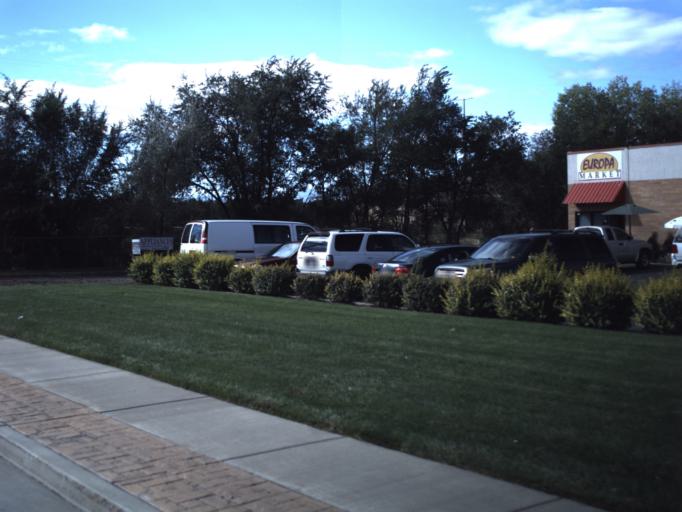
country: US
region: Utah
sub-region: Salt Lake County
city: Taylorsville
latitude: 40.7083
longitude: -111.9391
